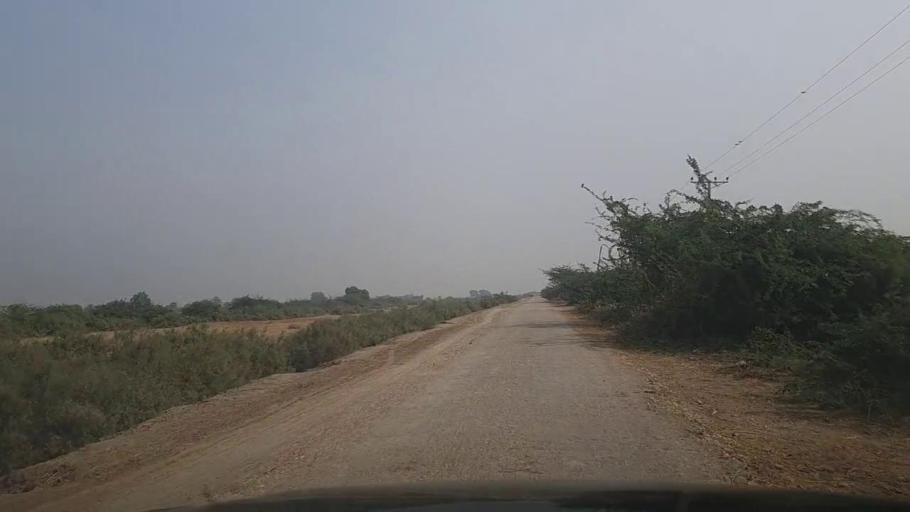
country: PK
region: Sindh
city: Mirpur Sakro
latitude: 24.4792
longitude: 67.6512
